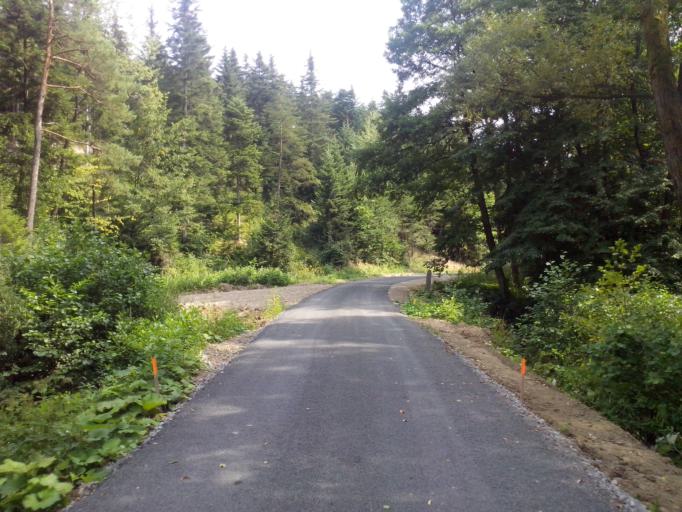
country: PL
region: Subcarpathian Voivodeship
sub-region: Powiat strzyzowski
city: Strzyzow
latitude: 49.8032
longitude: 21.8131
